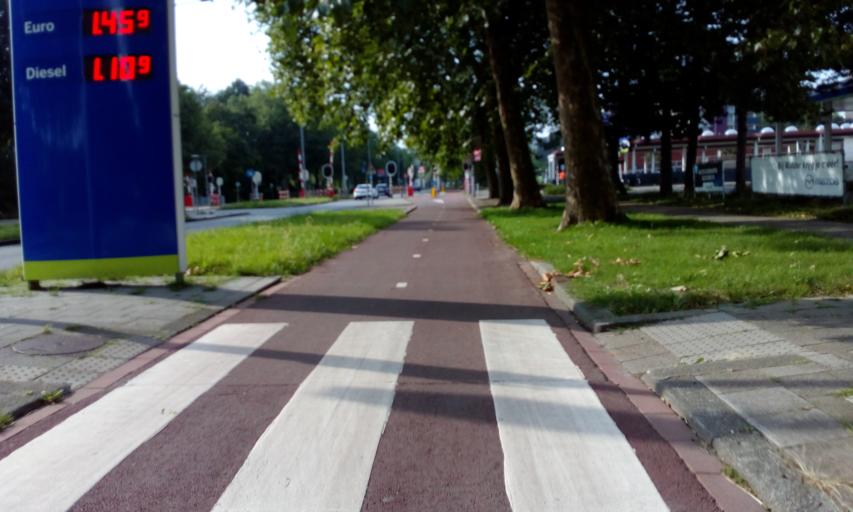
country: NL
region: South Holland
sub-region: Gemeente Rotterdam
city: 's-Gravenland
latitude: 51.9641
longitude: 4.5544
